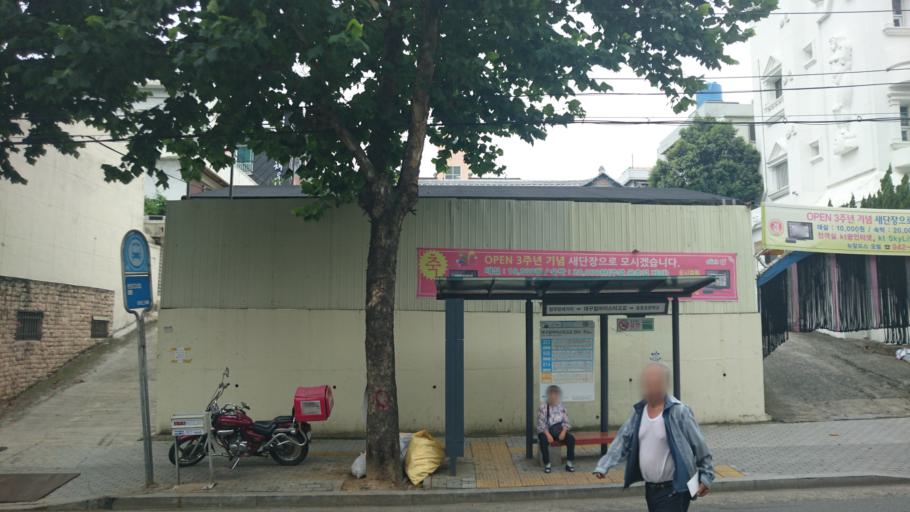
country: KR
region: Daegu
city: Daegu
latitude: 35.8810
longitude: 128.6473
